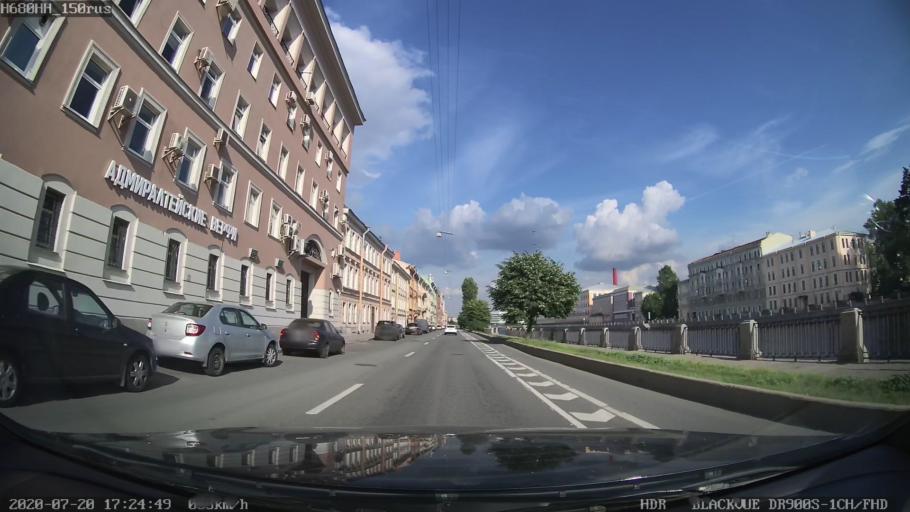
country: RU
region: St.-Petersburg
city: Admiralteisky
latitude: 59.9166
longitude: 30.2840
